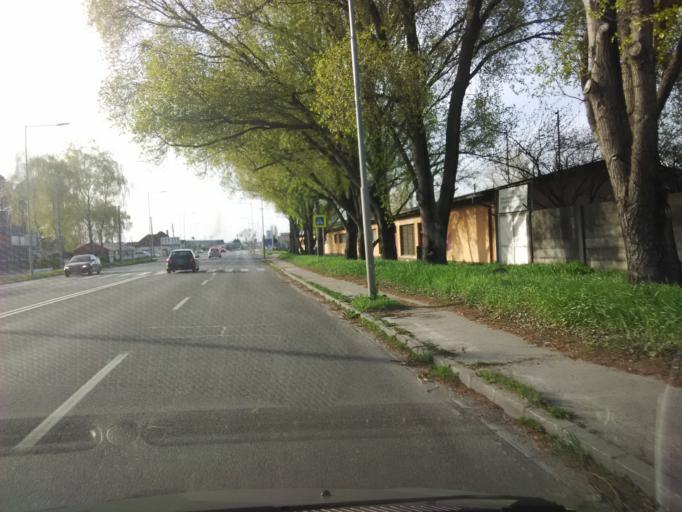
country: SK
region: Nitriansky
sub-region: Okres Nove Zamky
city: Nove Zamky
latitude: 48.0010
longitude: 18.1613
